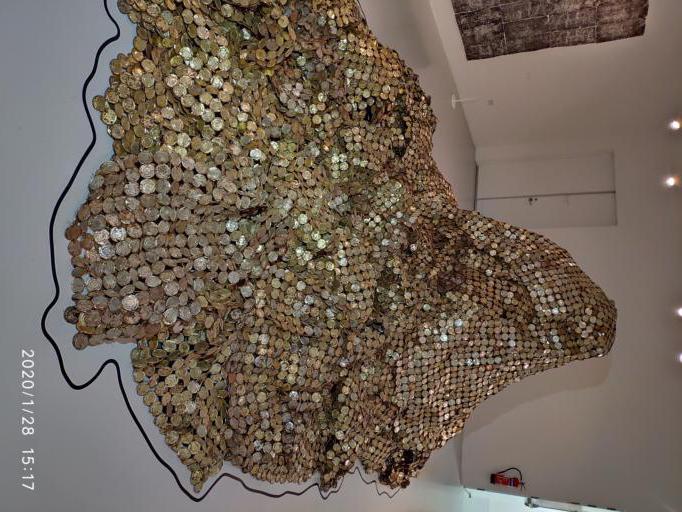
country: QA
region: Baladiyat ar Rayyan
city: Ar Rayyan
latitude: 25.3107
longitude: 51.4197
